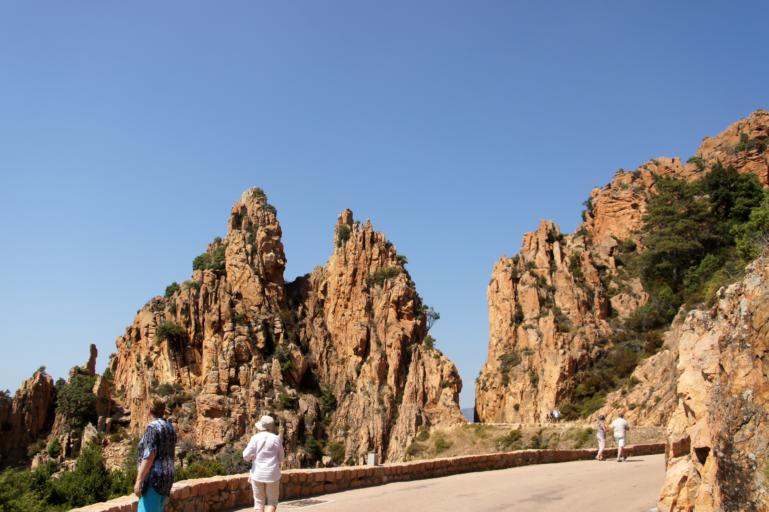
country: FR
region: Corsica
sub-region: Departement de la Corse-du-Sud
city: Cargese
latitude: 42.2453
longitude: 8.6536
